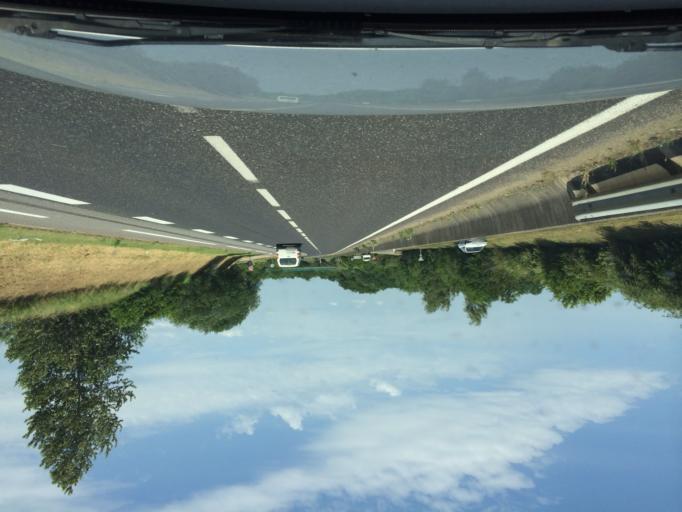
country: FR
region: Champagne-Ardenne
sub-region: Departement de la Haute-Marne
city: Bienville
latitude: 48.6408
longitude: 5.1270
